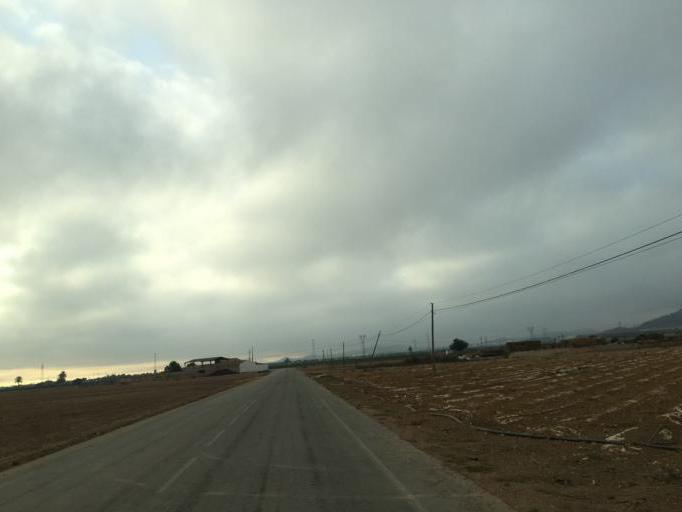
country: ES
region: Murcia
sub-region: Murcia
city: Cartagena
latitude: 37.6633
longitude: -0.9474
